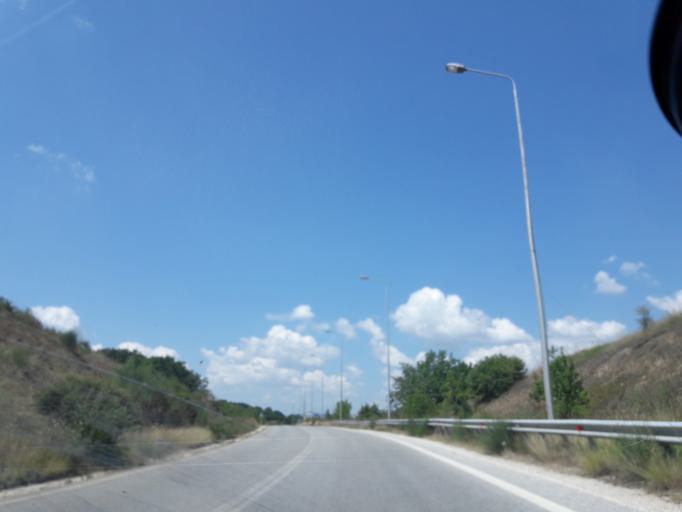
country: GR
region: Central Macedonia
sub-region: Nomos Chalkidikis
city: Polygyros
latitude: 40.4548
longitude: 23.4111
